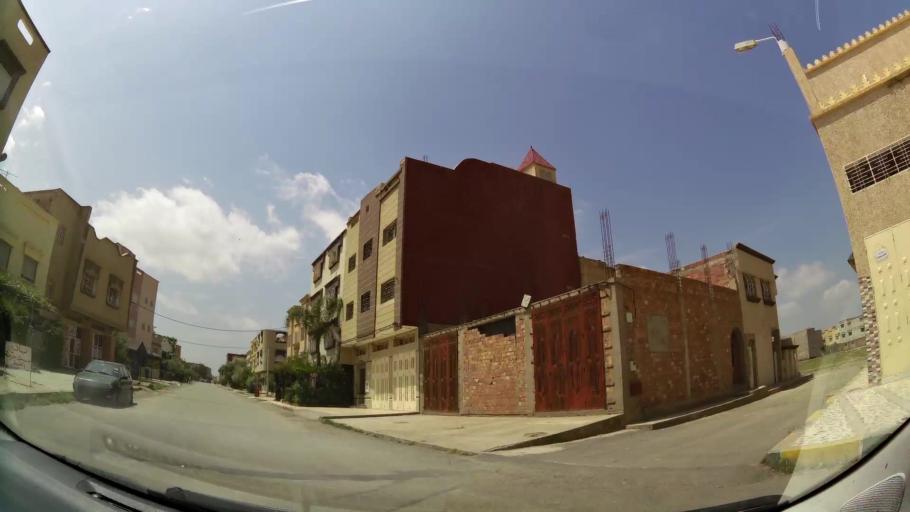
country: MA
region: Oriental
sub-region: Oujda-Angad
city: Oujda
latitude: 34.6889
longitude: -1.8863
